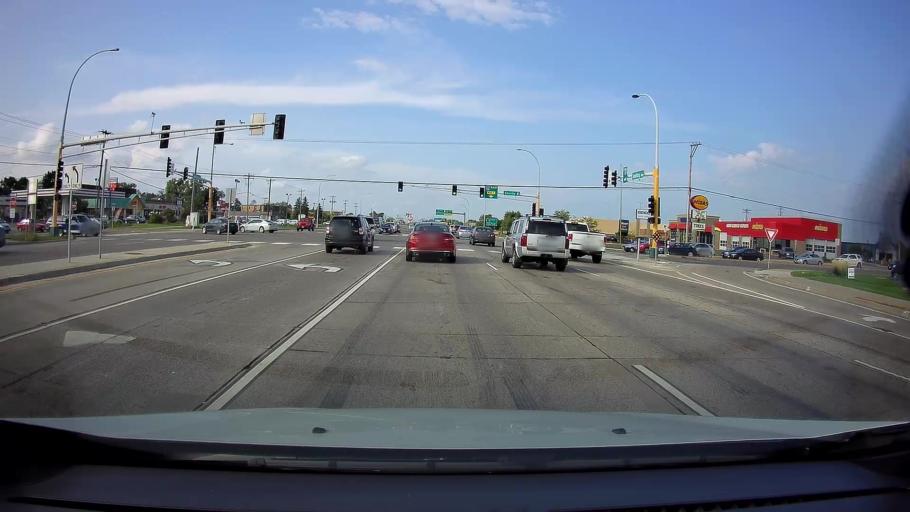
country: US
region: Minnesota
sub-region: Ramsey County
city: Roseville
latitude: 45.0059
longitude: -93.1661
